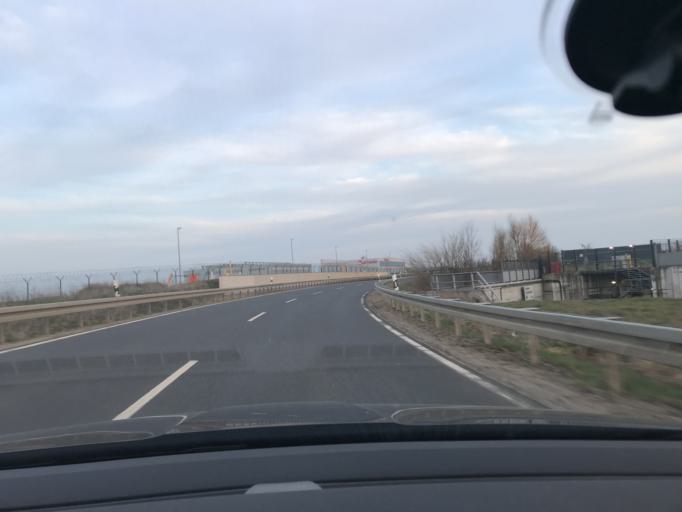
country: DE
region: Brandenburg
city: Schonefeld
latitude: 52.3624
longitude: 13.4761
